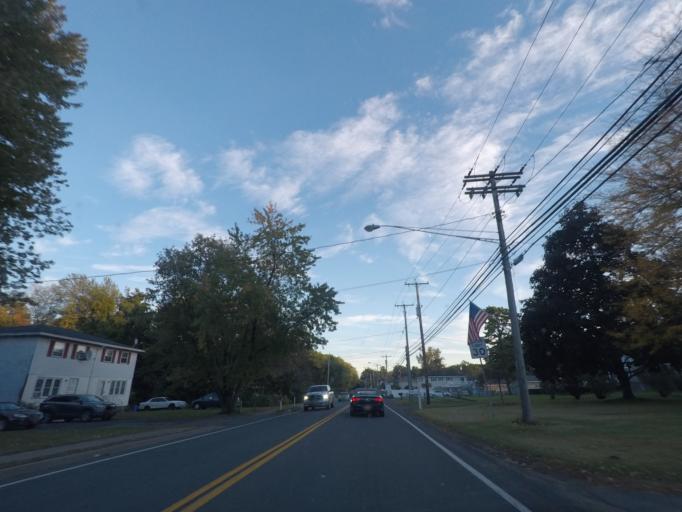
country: US
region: New York
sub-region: Albany County
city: Colonie
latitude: 42.7264
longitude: -73.8239
